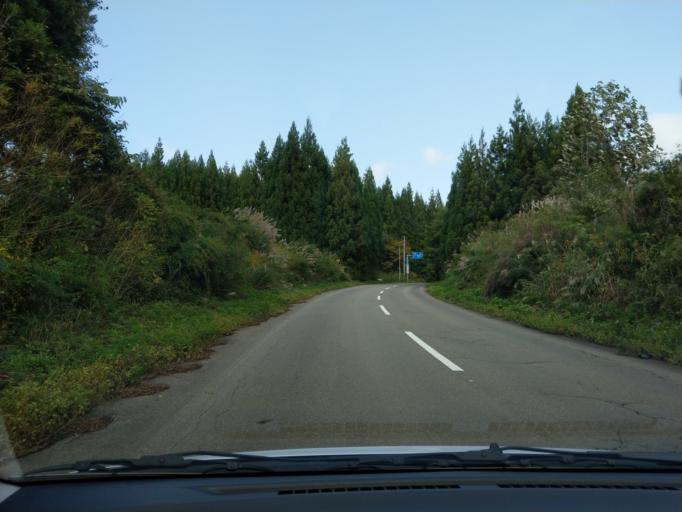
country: JP
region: Akita
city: Omagari
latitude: 39.5215
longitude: 140.2963
